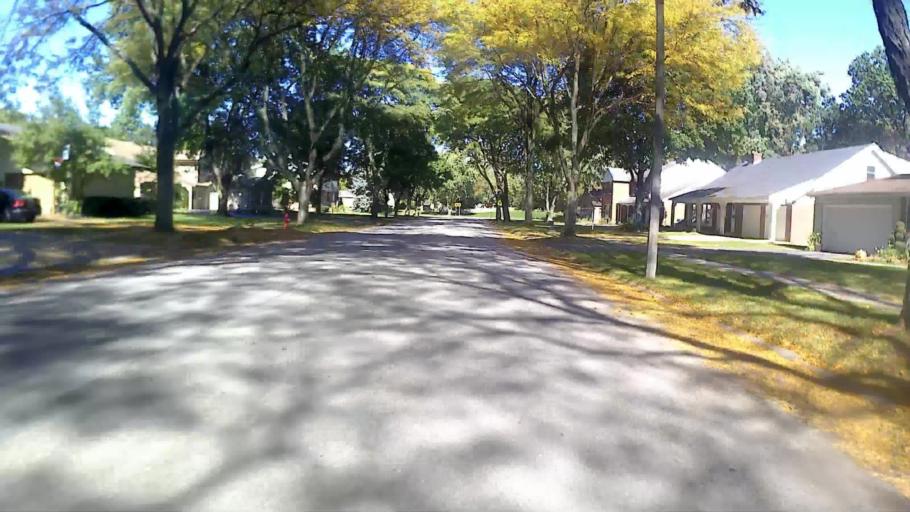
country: US
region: Illinois
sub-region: DuPage County
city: Itasca
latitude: 41.9770
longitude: -88.0131
